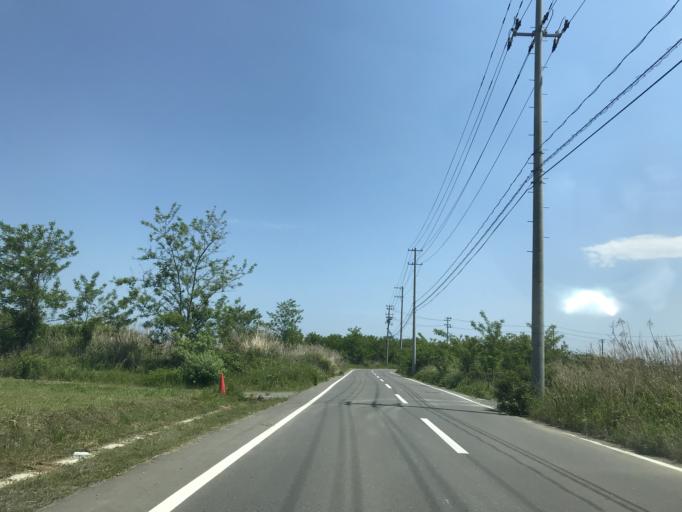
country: JP
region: Miyagi
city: Yamoto
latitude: 38.3700
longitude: 141.1543
